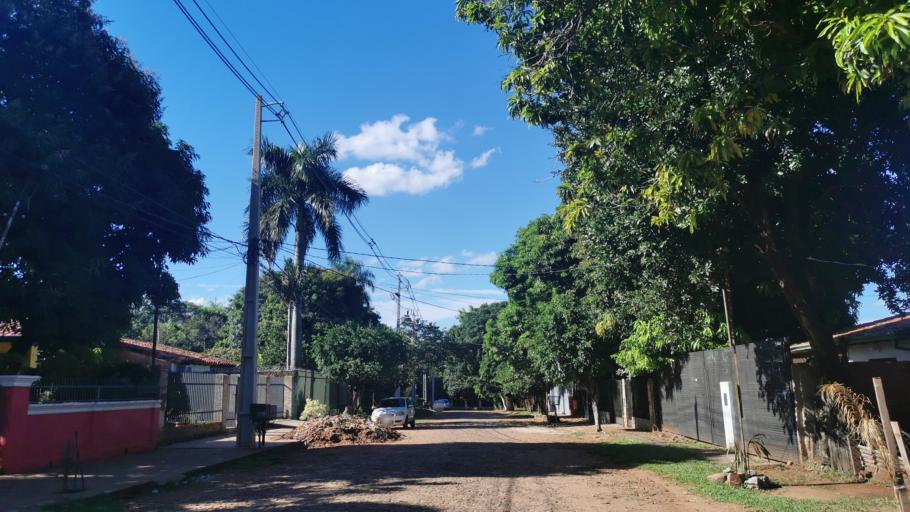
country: PY
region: Central
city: San Lorenzo
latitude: -25.3278
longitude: -57.5079
